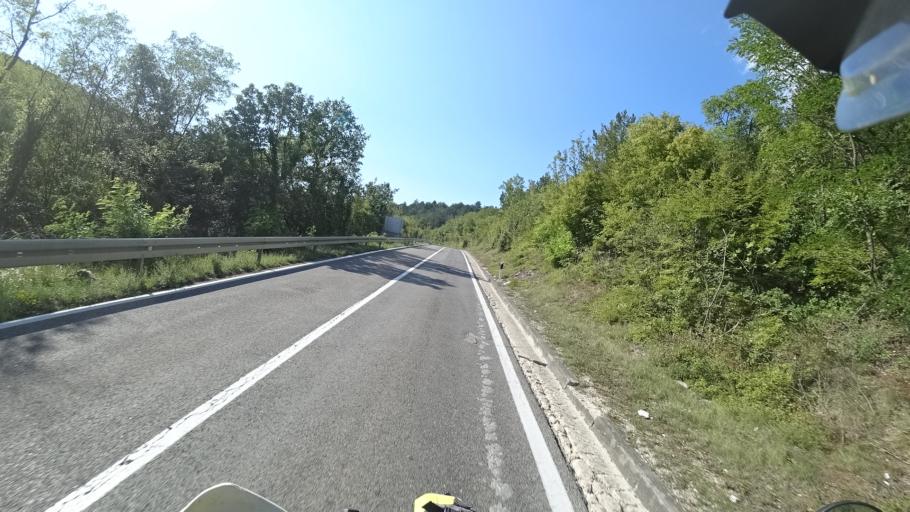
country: HR
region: Sibensko-Kniniska
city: Knin
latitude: 44.0196
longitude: 16.1952
